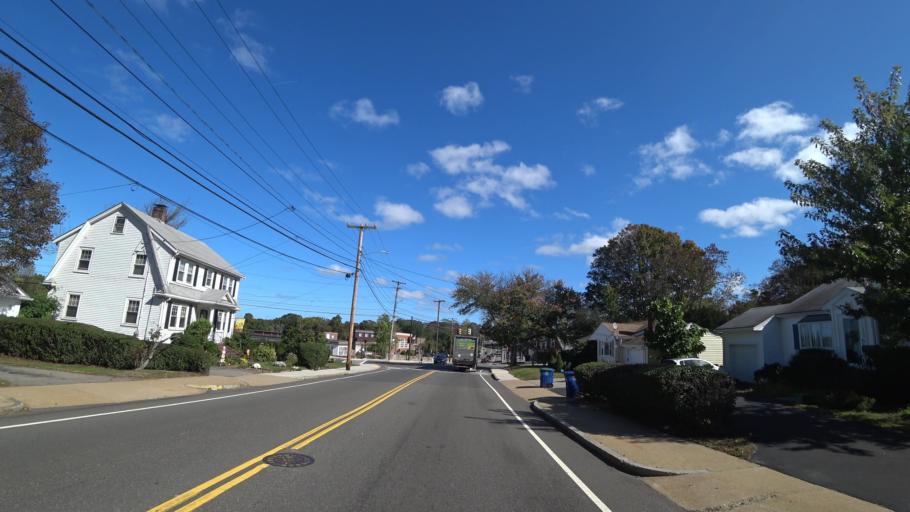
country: US
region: Massachusetts
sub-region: Norfolk County
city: Braintree
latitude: 42.2280
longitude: -70.9884
